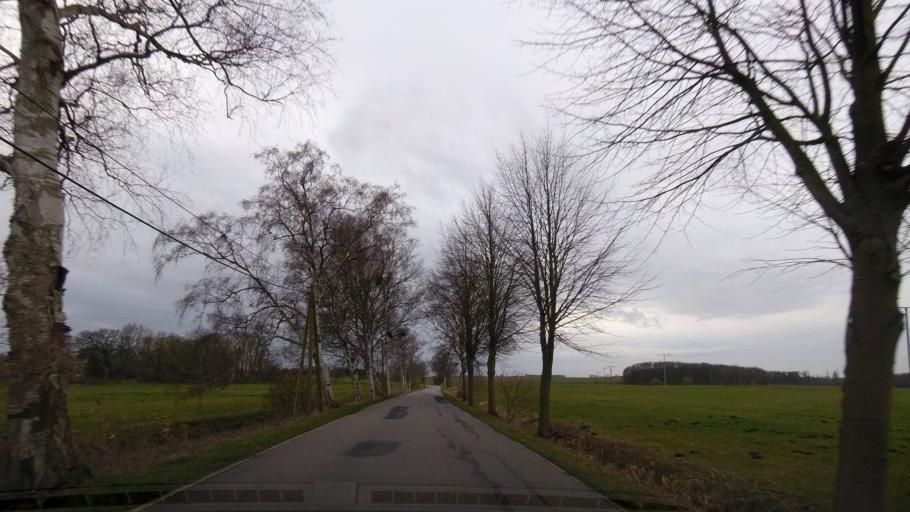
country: DE
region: Mecklenburg-Vorpommern
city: Robel
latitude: 53.4292
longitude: 12.5734
